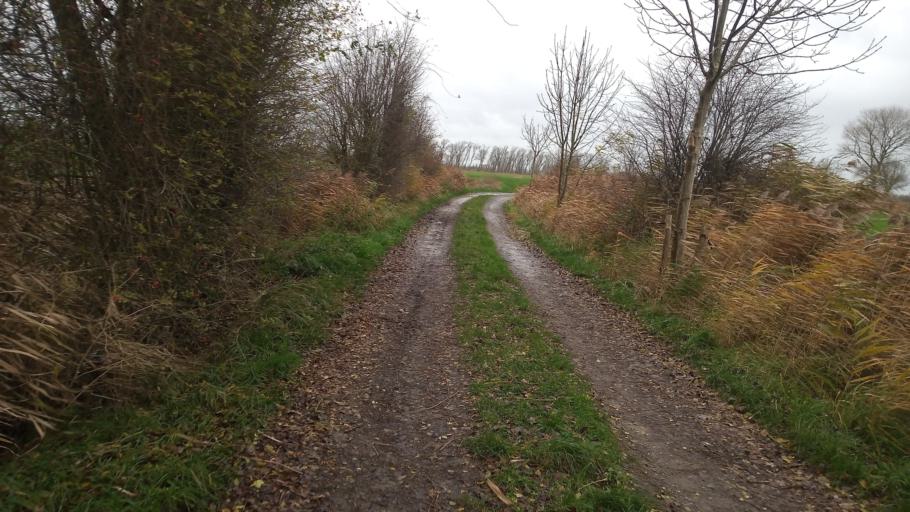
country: BE
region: Flanders
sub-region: Provincie West-Vlaanderen
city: Diksmuide
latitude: 51.0299
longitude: 2.9092
